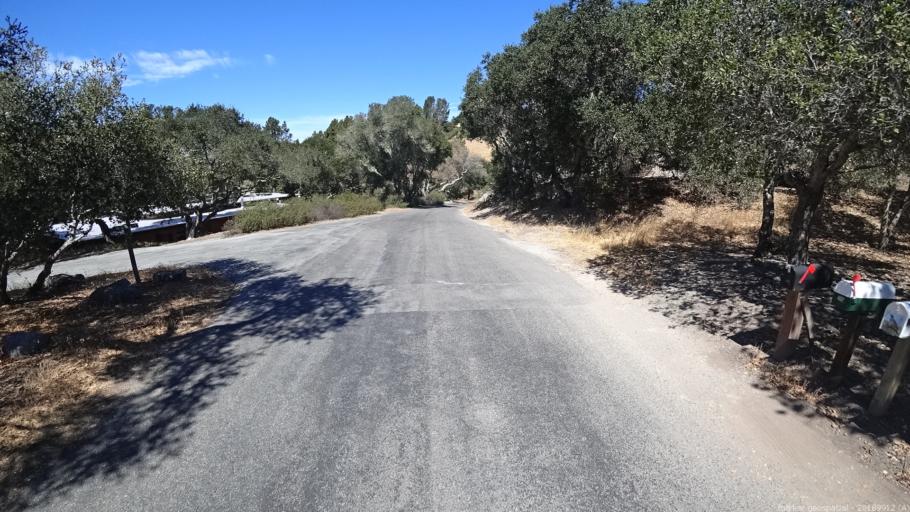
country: US
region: California
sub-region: Monterey County
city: Carmel Valley Village
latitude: 36.4859
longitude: -121.7213
